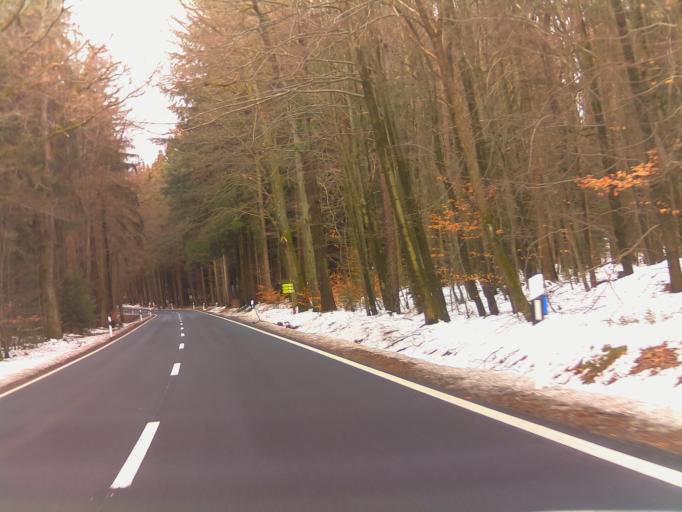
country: DE
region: Hesse
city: Michelstadt
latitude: 49.6654
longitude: 9.0750
